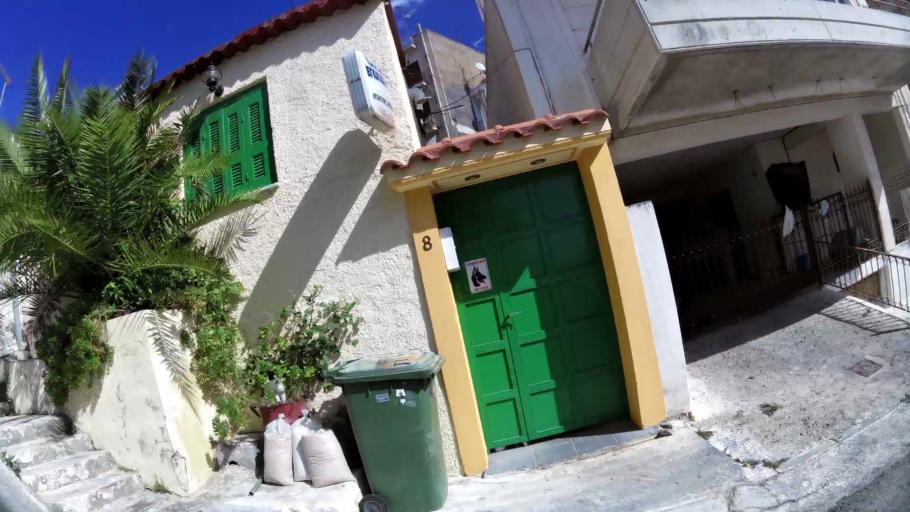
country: GR
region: Attica
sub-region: Nomos Piraios
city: Perama
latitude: 37.9658
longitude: 23.5799
